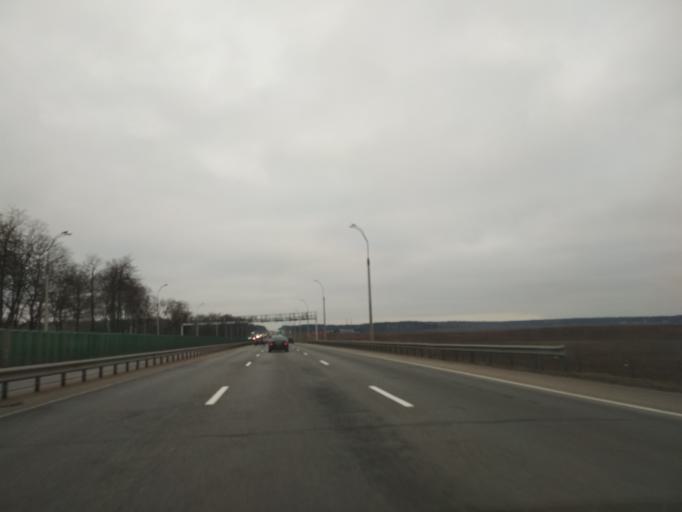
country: BY
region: Minsk
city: Vyaliki Trastsyanets
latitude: 53.8391
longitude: 27.7245
